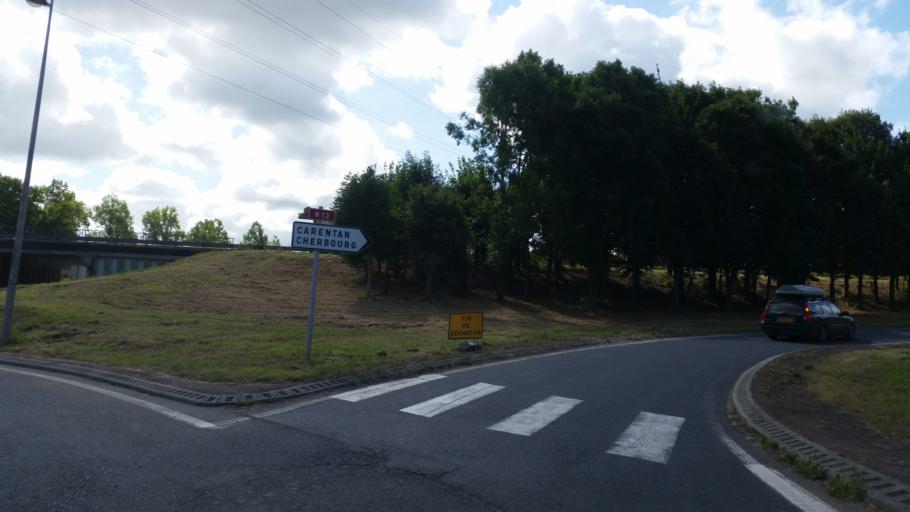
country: FR
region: Lower Normandy
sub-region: Departement du Calvados
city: Isigny-sur-Mer
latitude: 49.3118
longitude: -1.0985
